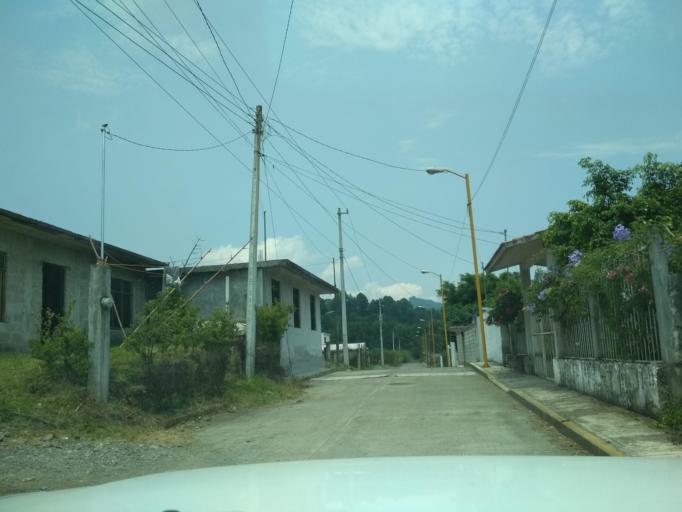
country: MX
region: Veracruz
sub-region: Mariano Escobedo
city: Mariano Escobedo
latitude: 18.9097
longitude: -97.1269
